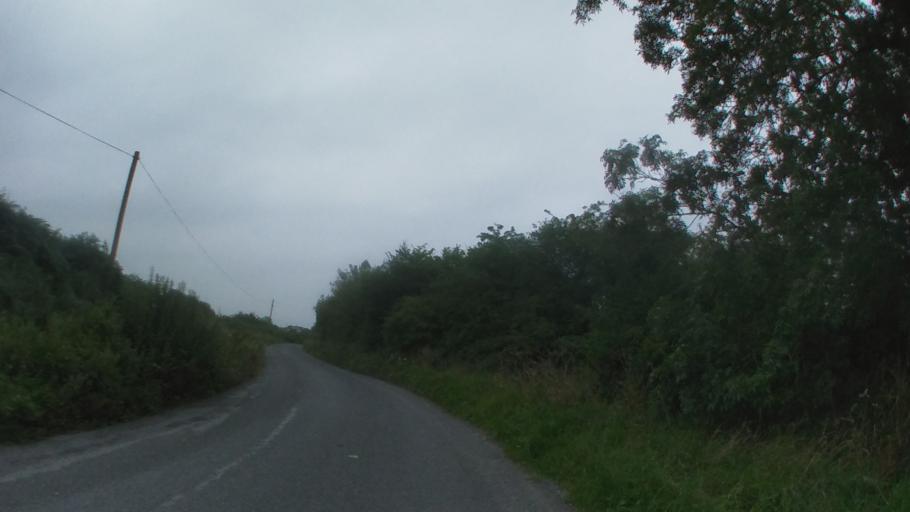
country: IE
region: Leinster
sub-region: Kilkenny
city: Kilkenny
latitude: 52.7012
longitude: -7.1928
